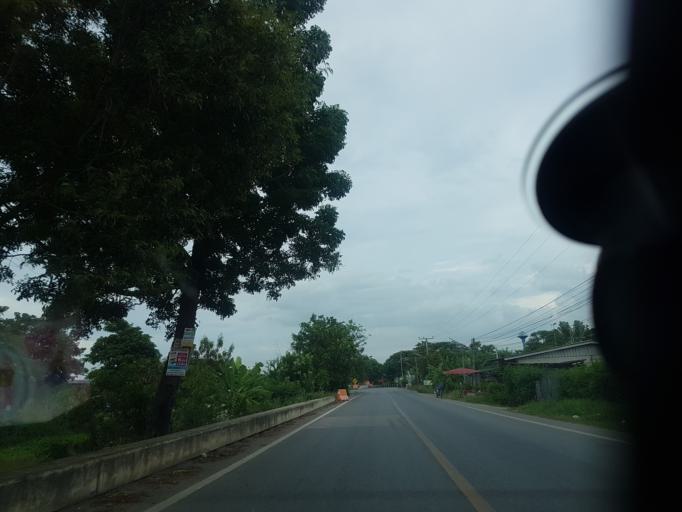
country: TH
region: Sara Buri
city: Nong Khae
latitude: 14.2749
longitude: 100.8896
